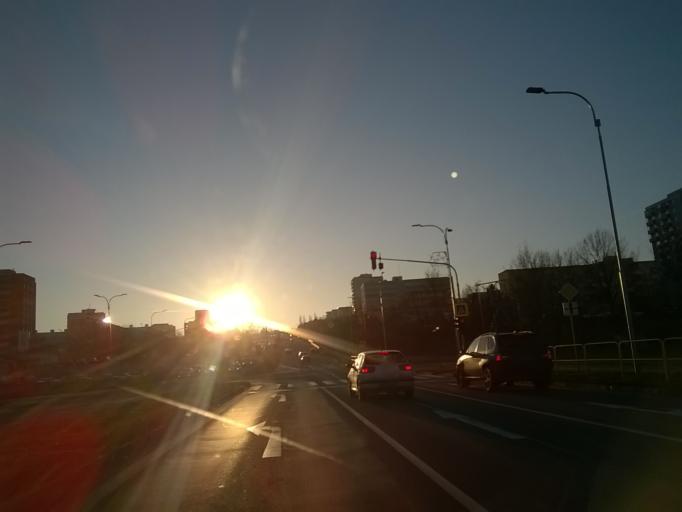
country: SK
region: Nitriansky
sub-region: Okres Nitra
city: Nitra
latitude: 48.3026
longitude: 18.0629
